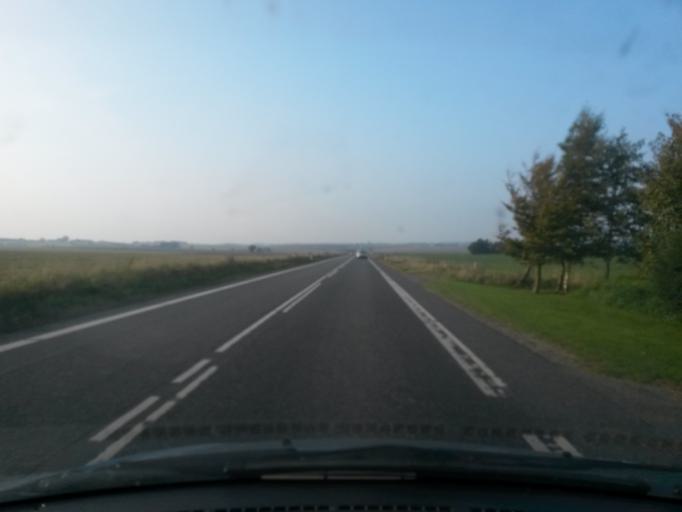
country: DK
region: Central Jutland
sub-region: Randers Kommune
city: Assentoft
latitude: 56.4131
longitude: 10.2223
